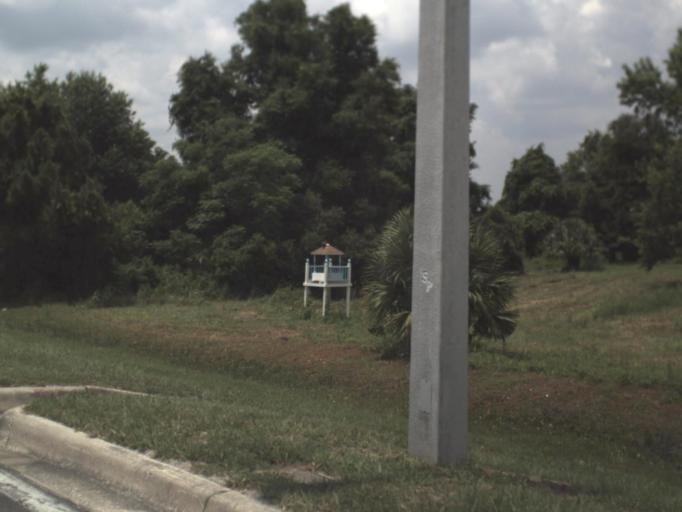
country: US
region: Florida
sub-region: Putnam County
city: Palatka
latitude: 29.6390
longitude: -81.6772
